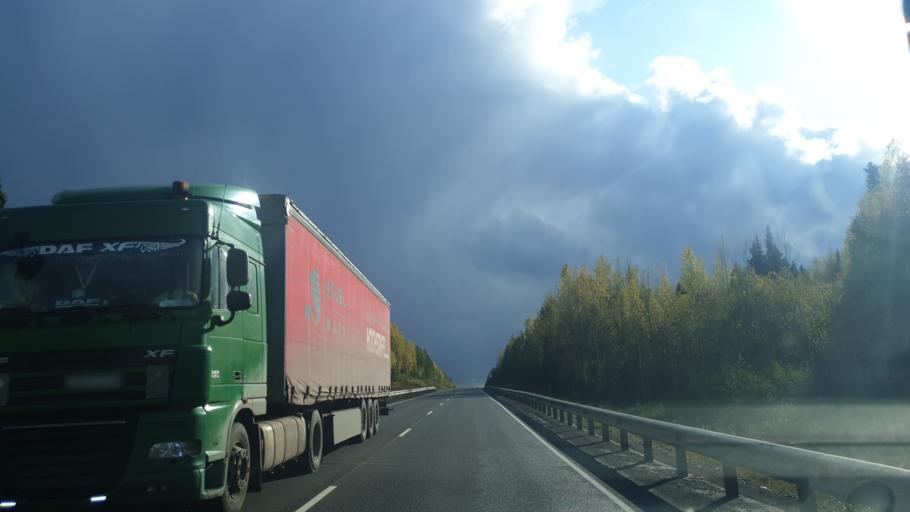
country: RU
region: Komi Republic
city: Vizinga
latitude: 60.7243
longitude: 49.4955
